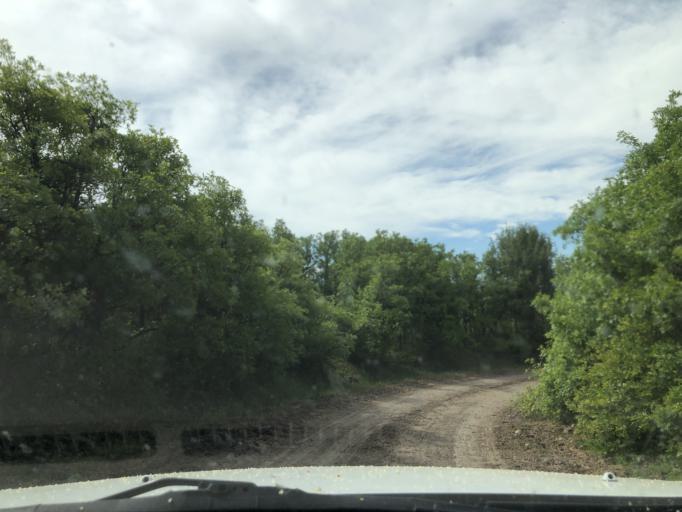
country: US
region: Colorado
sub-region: Delta County
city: Paonia
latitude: 39.0256
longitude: -107.3442
